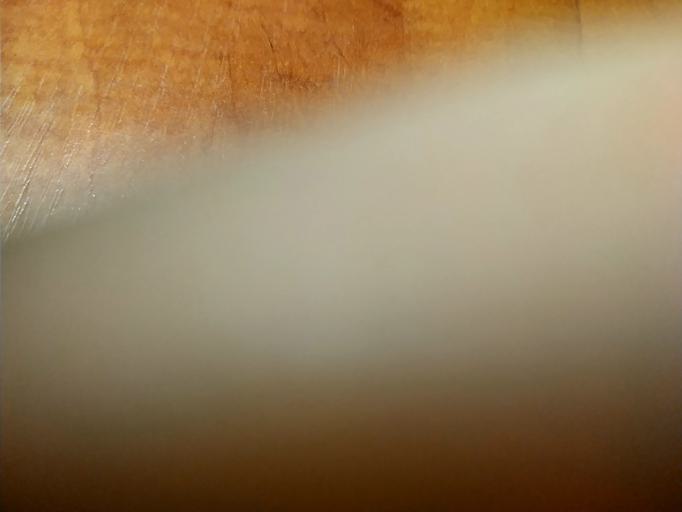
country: RU
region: Moskovskaya
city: Meshcherino
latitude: 55.2758
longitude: 38.3320
